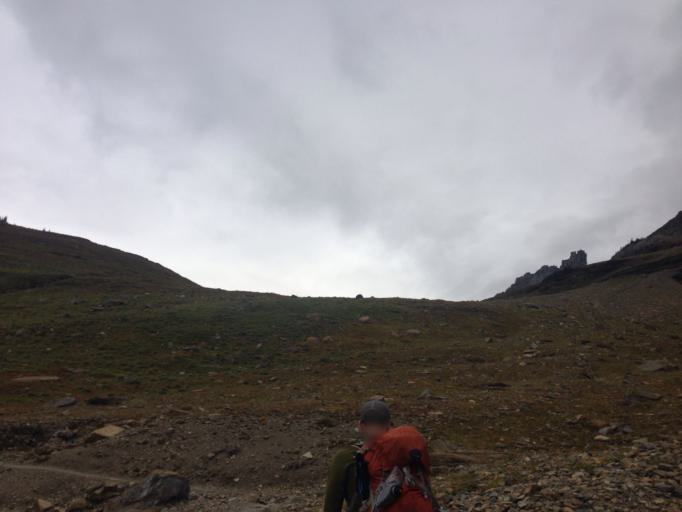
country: US
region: Montana
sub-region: Flathead County
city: Columbia Falls
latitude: 48.7343
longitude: -113.7228
